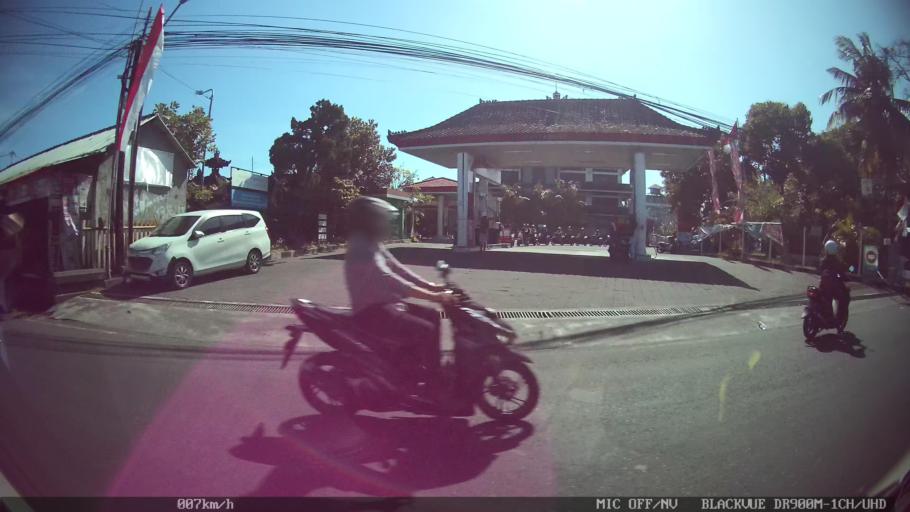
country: ID
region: Bali
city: Denpasar
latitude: -8.6491
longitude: 115.1865
